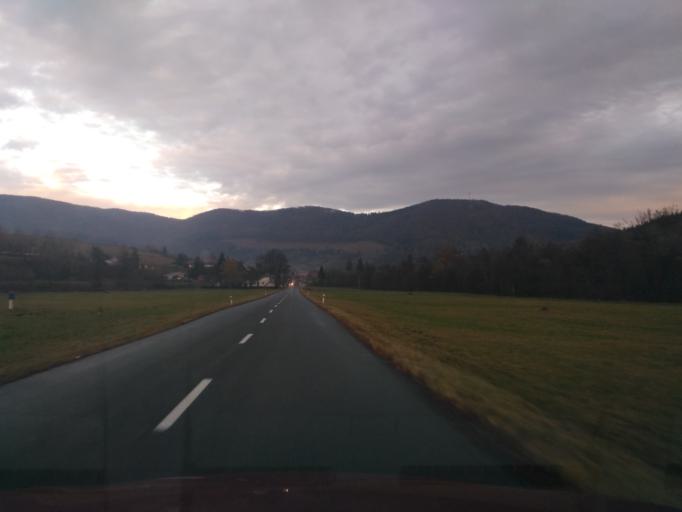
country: SK
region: Kosicky
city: Gelnica
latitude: 48.8251
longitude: 20.8569
